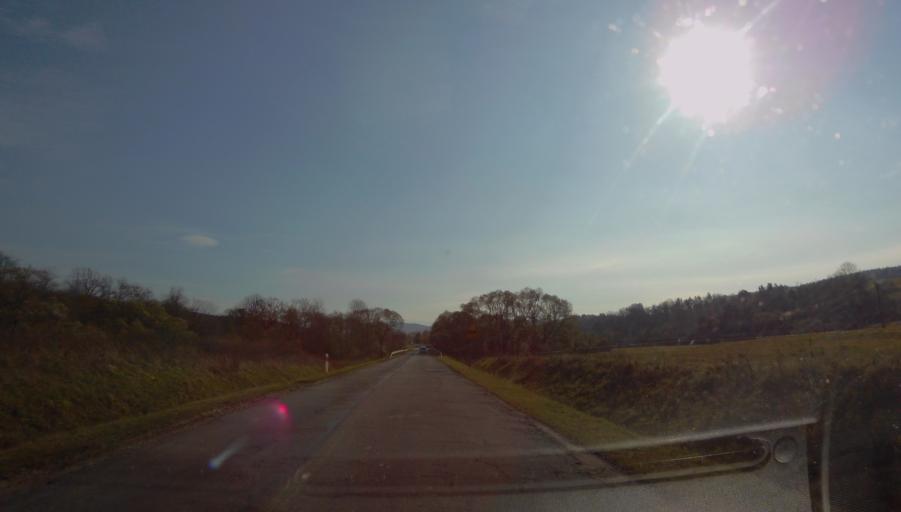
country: PL
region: Subcarpathian Voivodeship
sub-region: Powiat sanocki
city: Komancza
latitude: 49.2446
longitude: 22.1306
